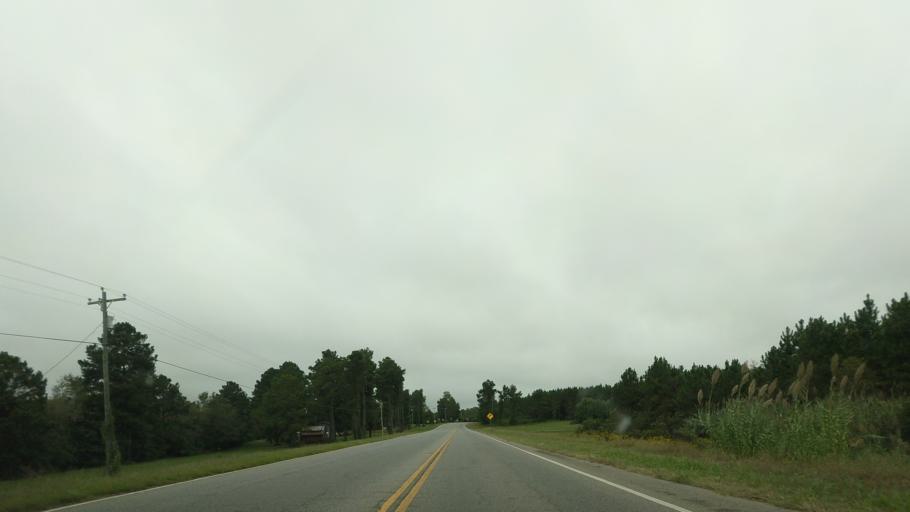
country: US
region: Georgia
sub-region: Irwin County
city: Ocilla
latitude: 31.6508
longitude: -83.2447
